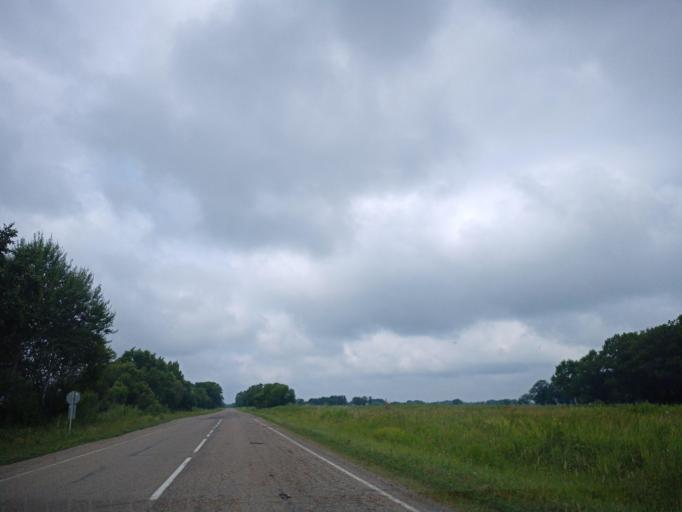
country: RU
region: Primorskiy
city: Dal'nerechensk
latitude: 45.9484
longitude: 133.9064
